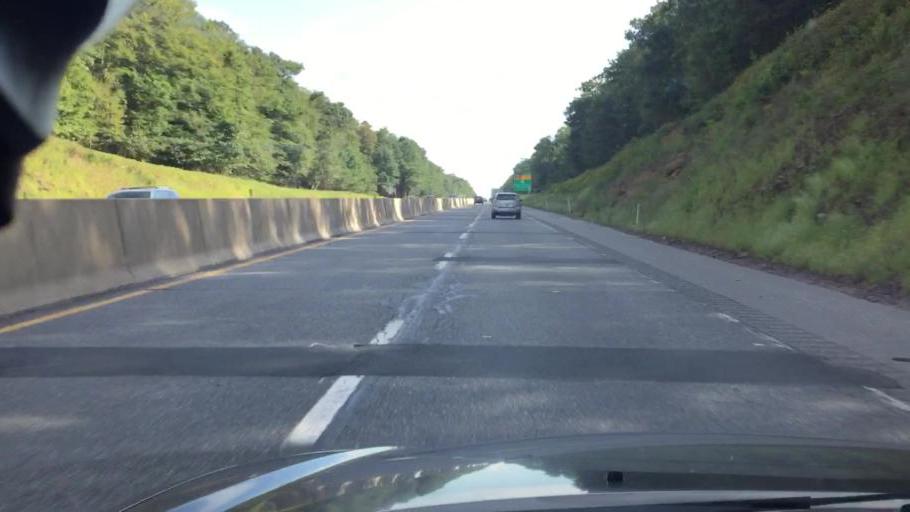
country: US
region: Pennsylvania
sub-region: Carbon County
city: Towamensing Trails
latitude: 41.0023
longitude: -75.6346
